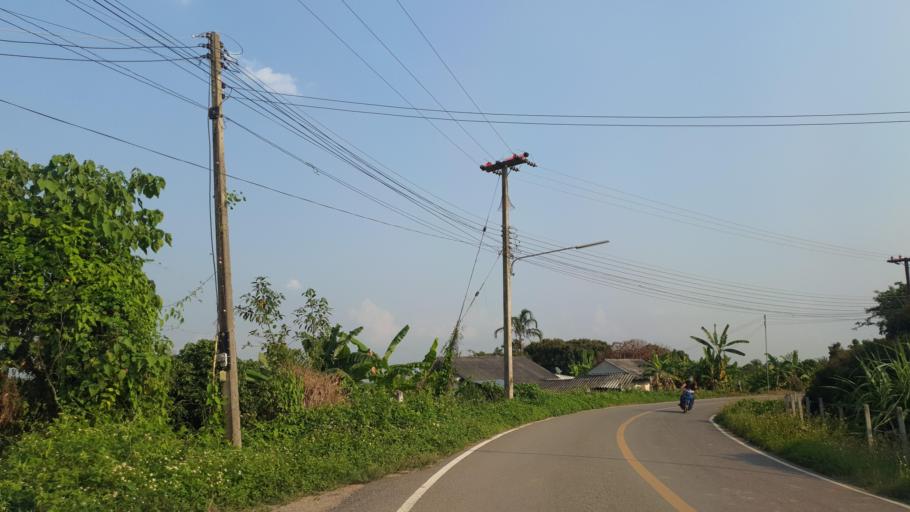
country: TH
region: Chiang Mai
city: Mae Wang
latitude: 18.6536
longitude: 98.8165
